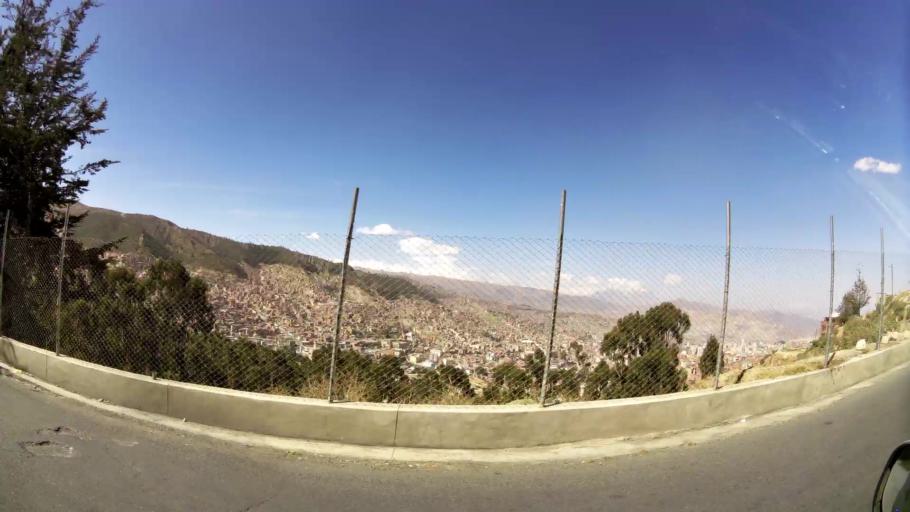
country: BO
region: La Paz
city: La Paz
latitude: -16.4866
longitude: -68.1550
